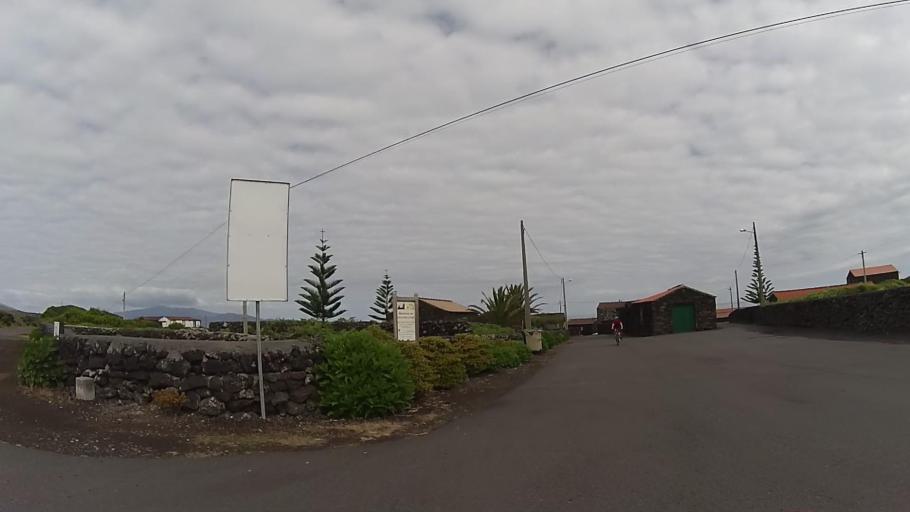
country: PT
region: Azores
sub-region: Madalena
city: Madalena
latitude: 38.5548
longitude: -28.4457
